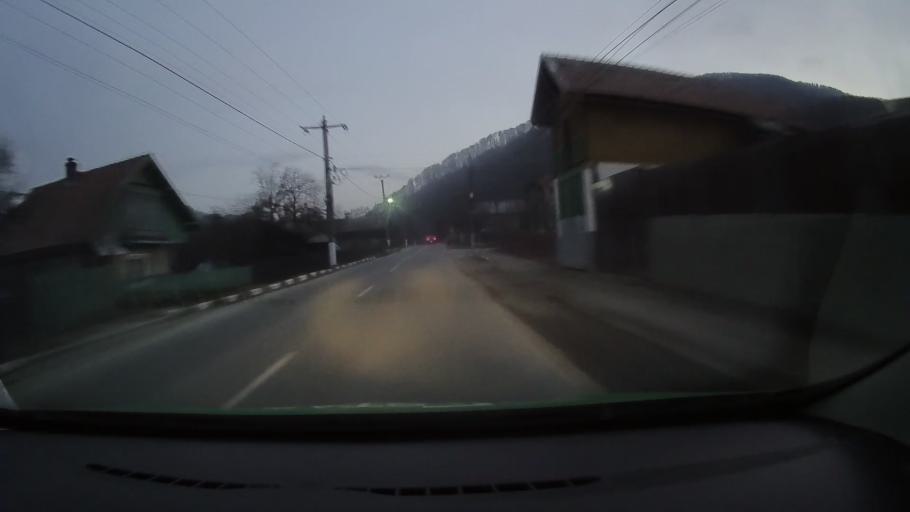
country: RO
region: Prahova
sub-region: Comuna Valea Doftanei
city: Tesila
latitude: 45.2883
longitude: 25.7232
